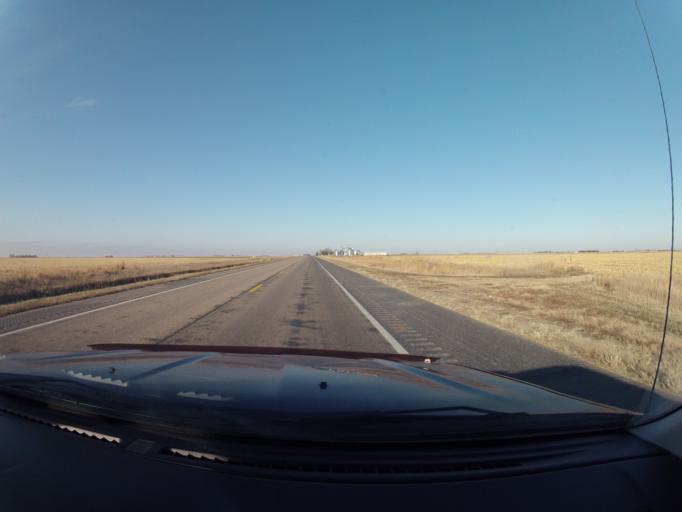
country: US
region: Nebraska
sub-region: Kearney County
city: Minden
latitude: 40.5210
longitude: -98.9518
